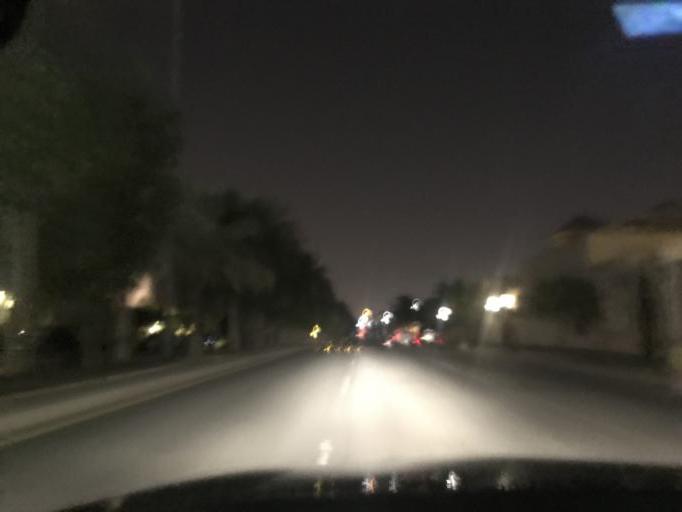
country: SA
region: Ar Riyad
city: Riyadh
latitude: 24.7129
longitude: 46.7782
